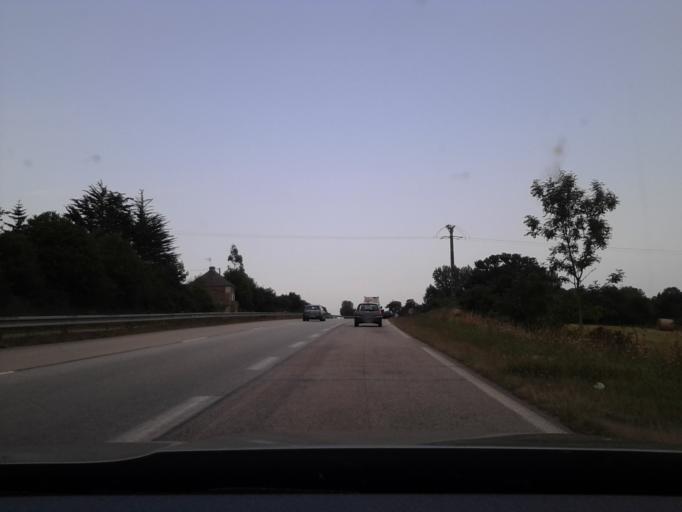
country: FR
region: Lower Normandy
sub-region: Departement de la Manche
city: Valognes
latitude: 49.5226
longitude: -1.5033
